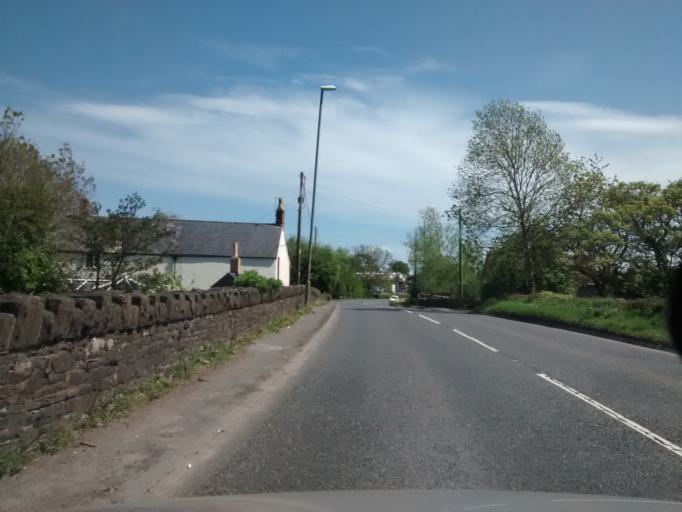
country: GB
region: England
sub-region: Bath and North East Somerset
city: Clutton
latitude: 51.3145
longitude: -2.5387
